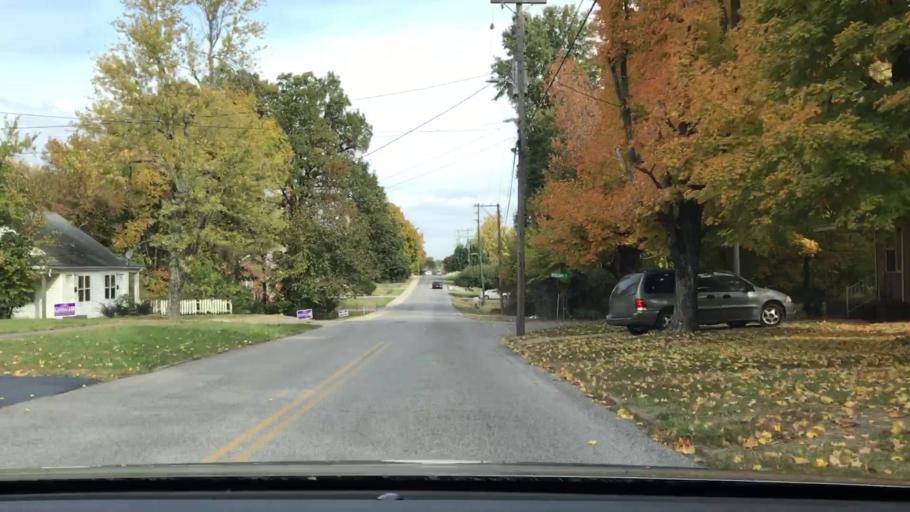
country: US
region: Kentucky
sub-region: Graves County
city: Mayfield
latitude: 36.7443
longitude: -88.6495
